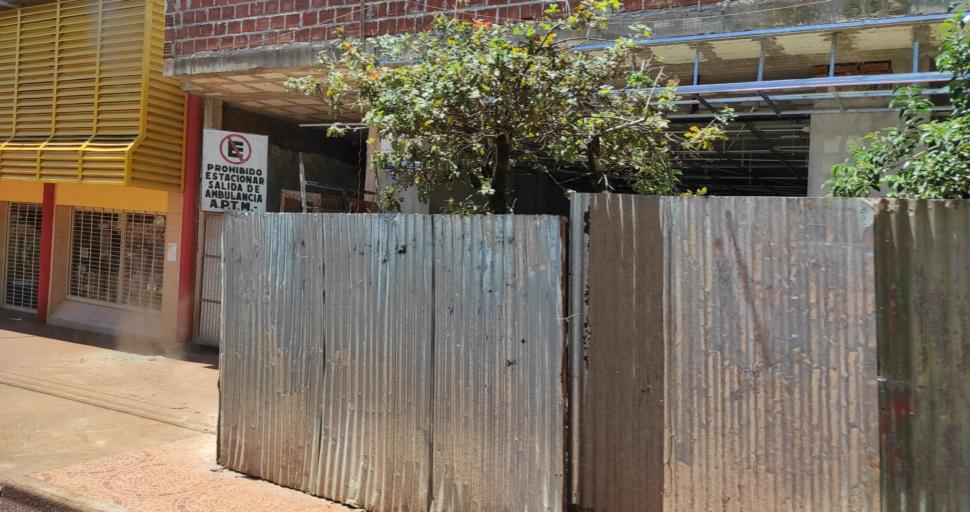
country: AR
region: Misiones
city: Dos de Mayo
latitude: -26.9931
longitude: -54.4798
